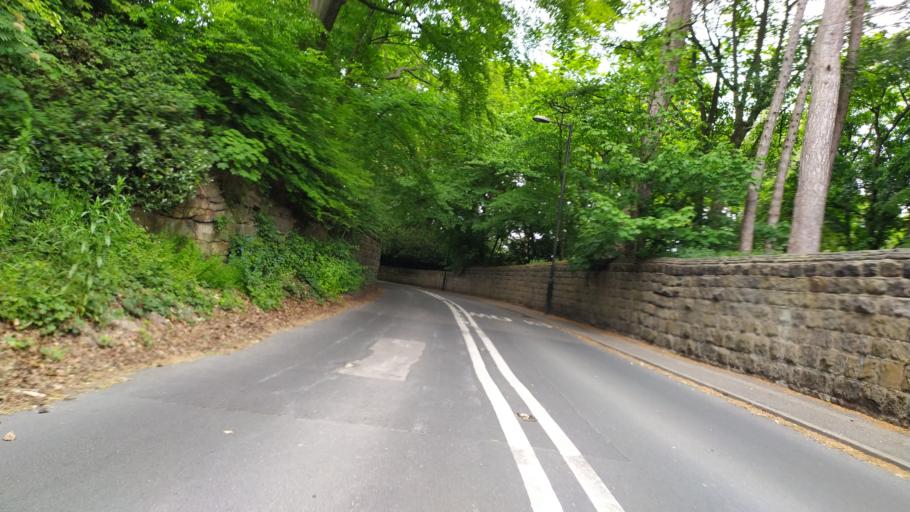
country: GB
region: England
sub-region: City and Borough of Leeds
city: Chapel Allerton
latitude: 53.8352
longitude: -1.5830
